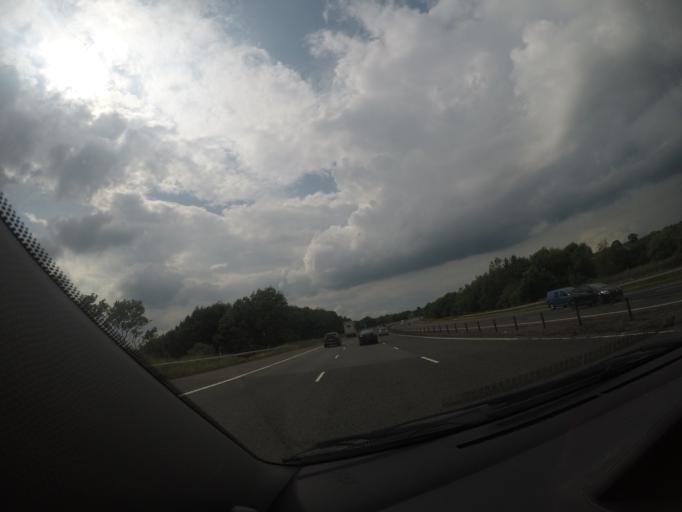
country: GB
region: Scotland
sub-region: Dumfries and Galloway
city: Annan
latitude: 55.0566
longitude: -3.2509
